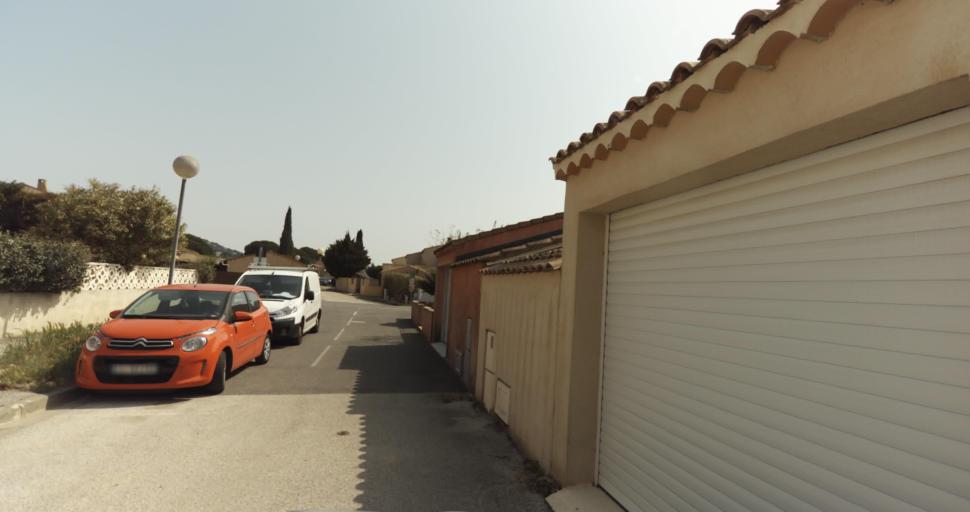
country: FR
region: Provence-Alpes-Cote d'Azur
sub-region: Departement du Var
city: Bormes-les-Mimosas
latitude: 43.1404
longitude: 6.3427
